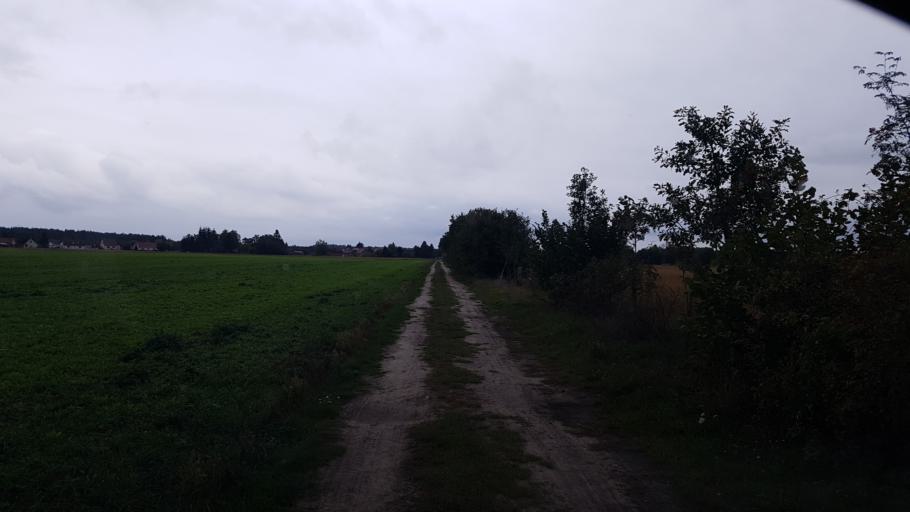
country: DE
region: Brandenburg
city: Finsterwalde
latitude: 51.5749
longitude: 13.6719
